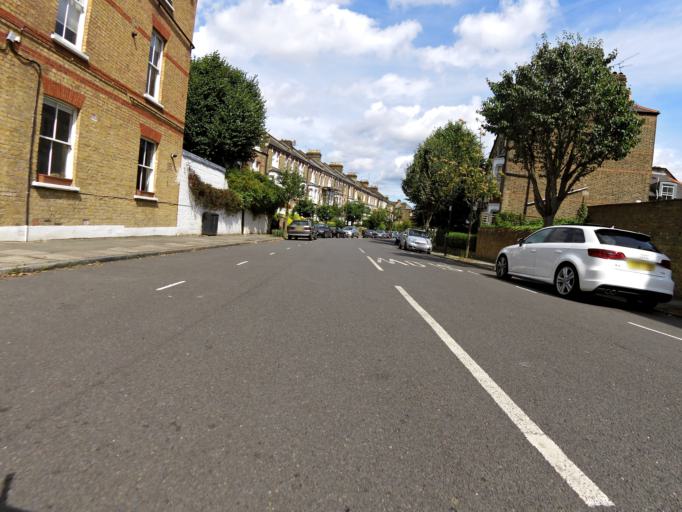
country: GB
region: England
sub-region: Greater London
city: Holloway
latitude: 51.5556
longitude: -0.1321
